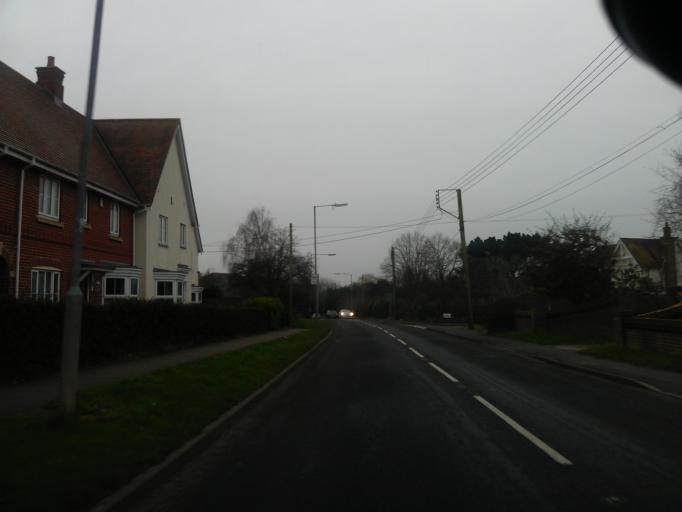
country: GB
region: England
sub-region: Essex
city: Tiptree
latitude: 51.8109
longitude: 0.7431
